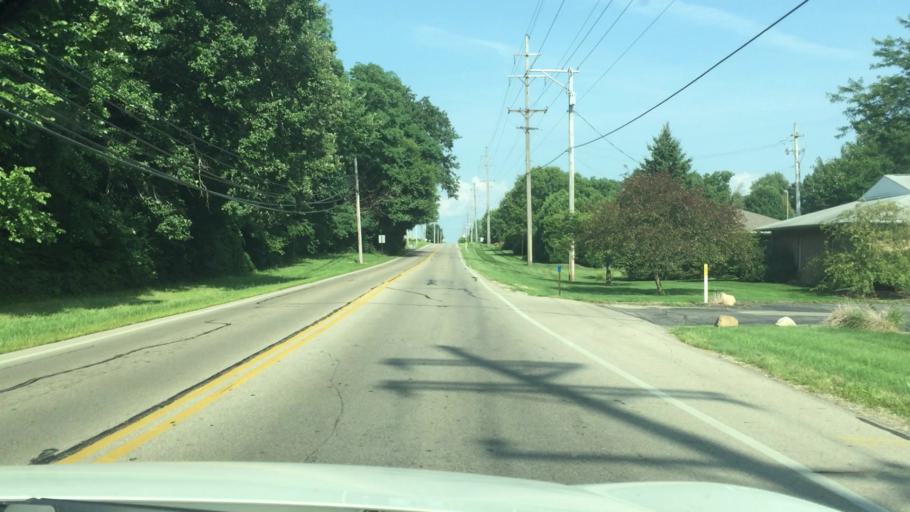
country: US
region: Ohio
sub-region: Clark County
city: Northridge
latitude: 39.9948
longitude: -83.7624
